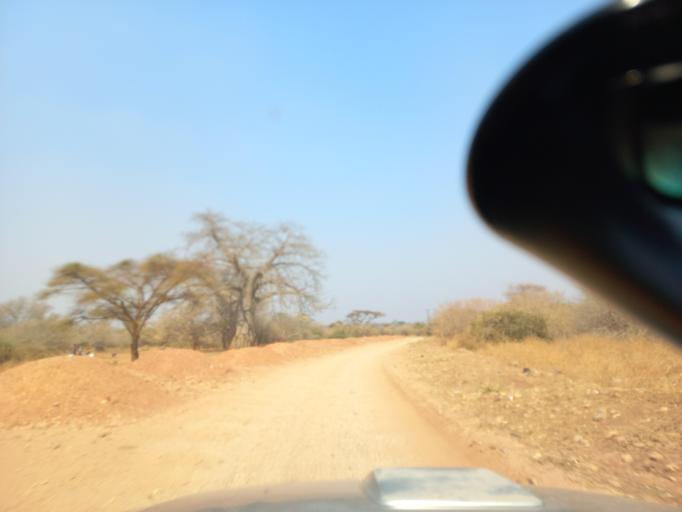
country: ZW
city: Chirundu
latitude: -15.9168
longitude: 28.9892
